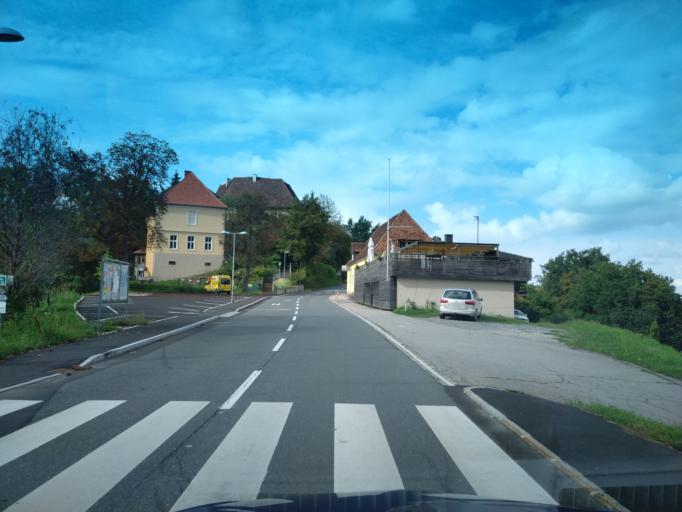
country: AT
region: Styria
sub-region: Politischer Bezirk Leibnitz
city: Seggauberg
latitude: 46.7776
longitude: 15.5243
